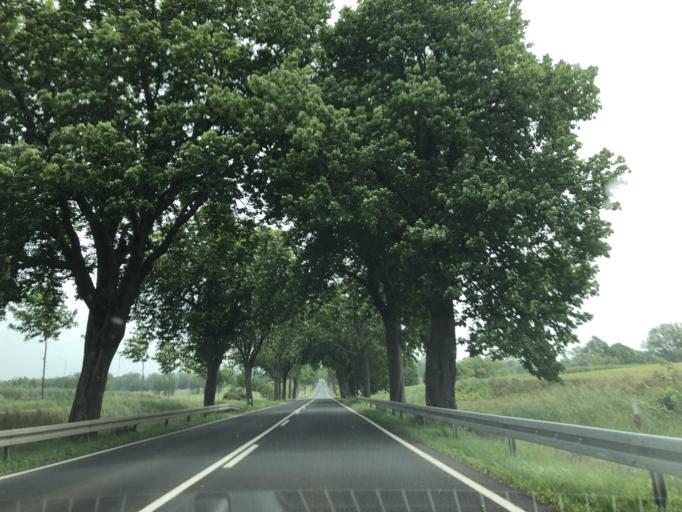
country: DE
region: Brandenburg
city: Gumtow
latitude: 52.9756
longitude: 12.2693
